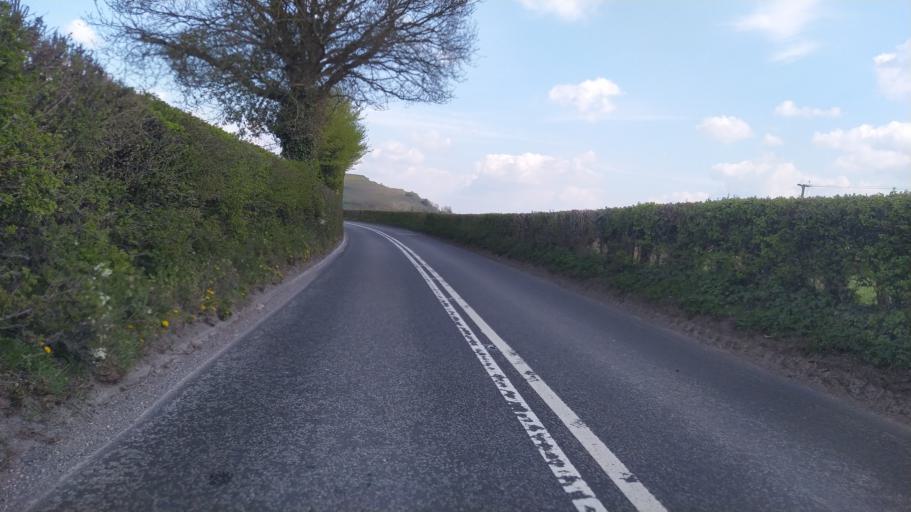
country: GB
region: England
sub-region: Wiltshire
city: Corsley
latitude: 51.2060
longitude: -2.2528
